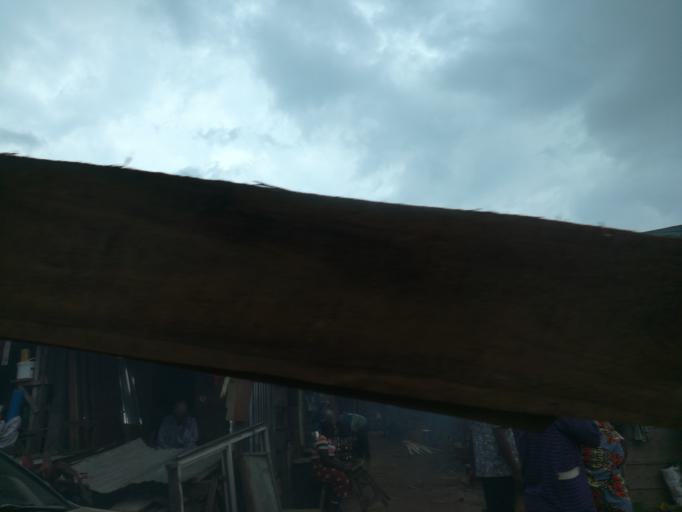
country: NG
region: Lagos
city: Oshodi
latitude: 6.5503
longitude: 3.3362
